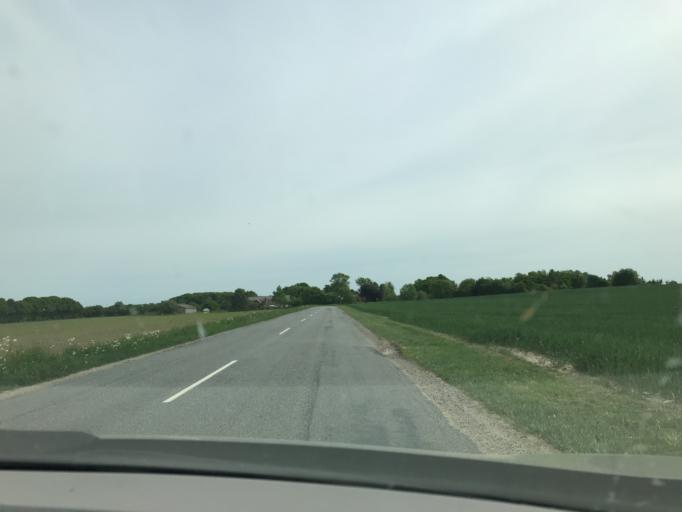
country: DK
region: Central Jutland
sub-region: Norddjurs Kommune
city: Allingabro
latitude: 56.5327
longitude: 10.3092
